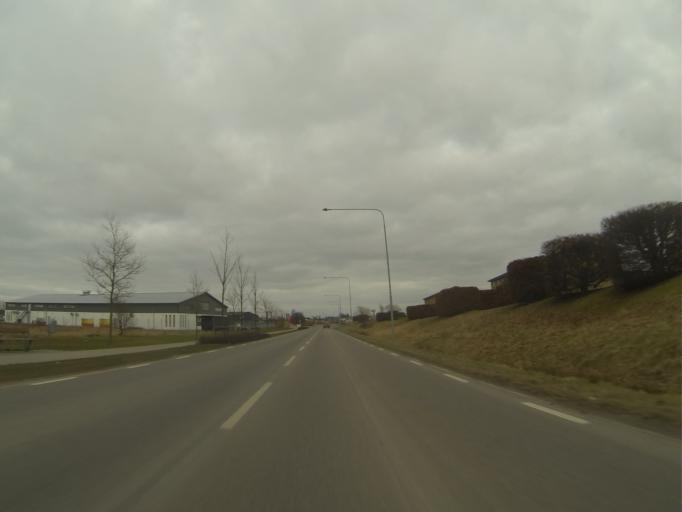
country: SE
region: Skane
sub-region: Svedala Kommun
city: Svedala
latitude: 55.5154
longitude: 13.2413
